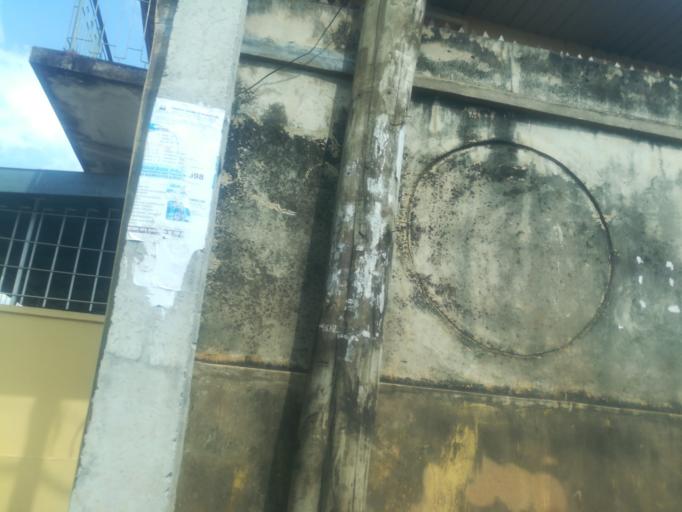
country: NG
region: Oyo
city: Ibadan
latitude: 7.3547
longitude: 3.8746
